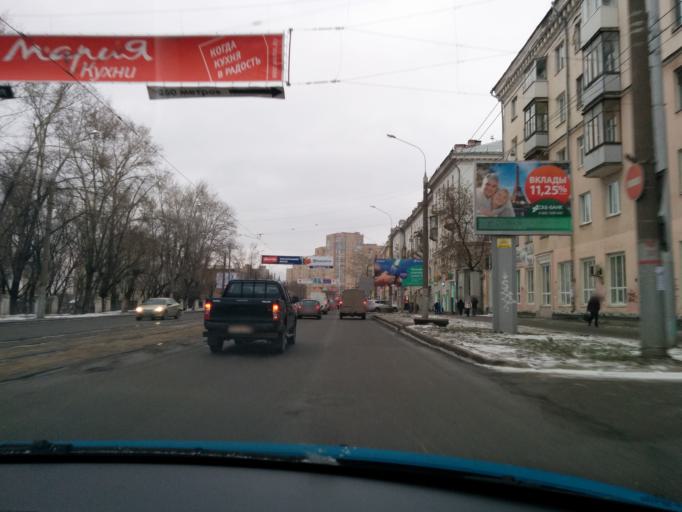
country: RU
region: Perm
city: Perm
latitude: 58.0202
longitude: 56.2790
